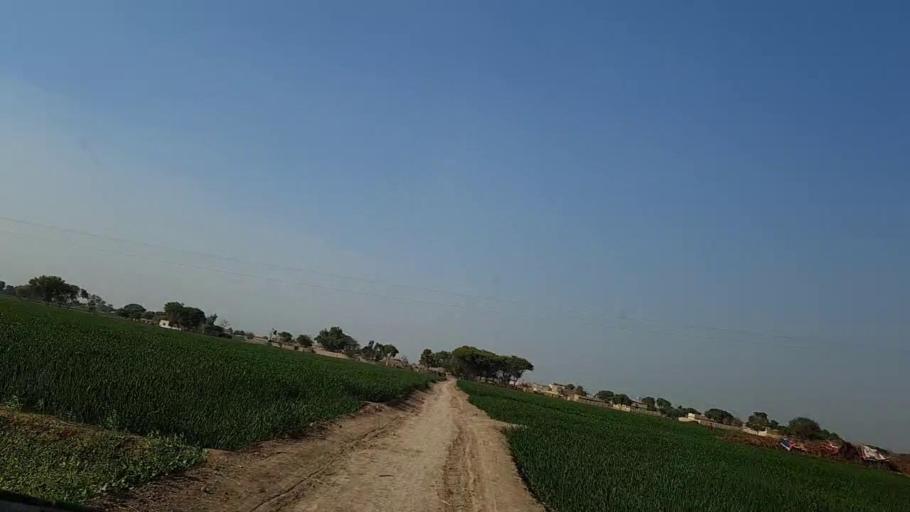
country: PK
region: Sindh
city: Sakrand
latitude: 26.1222
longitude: 68.2397
